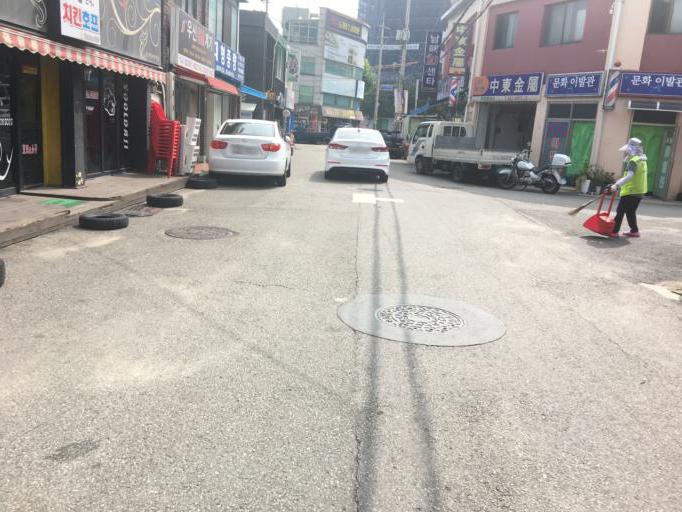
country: KR
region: Gyeonggi-do
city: Bucheon-si
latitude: 37.5135
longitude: 126.7741
